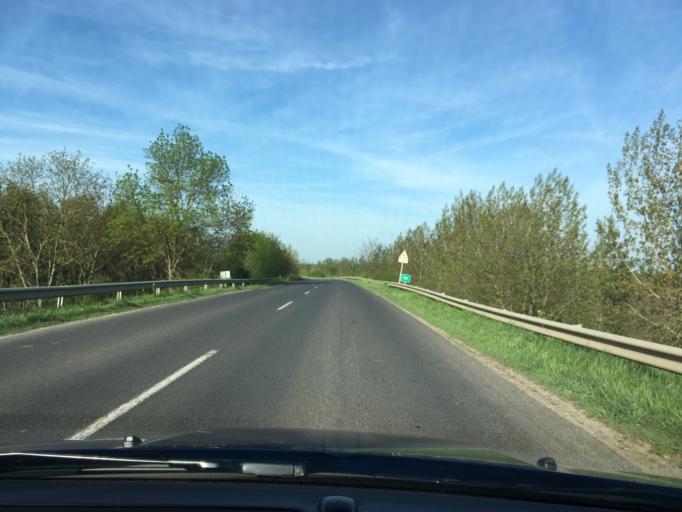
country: HU
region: Bekes
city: Korostarcsa
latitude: 46.8842
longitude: 21.0328
